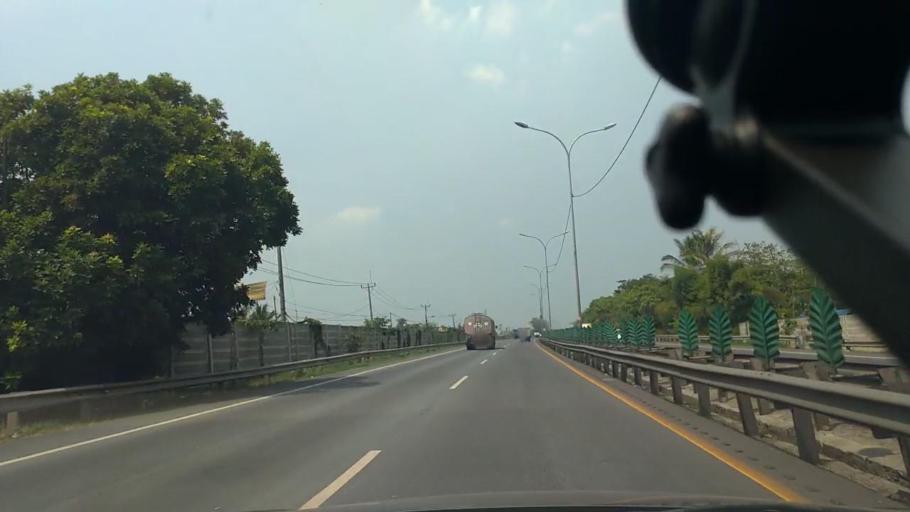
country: ID
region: Banten
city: Serang
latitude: -6.1001
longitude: 106.1716
